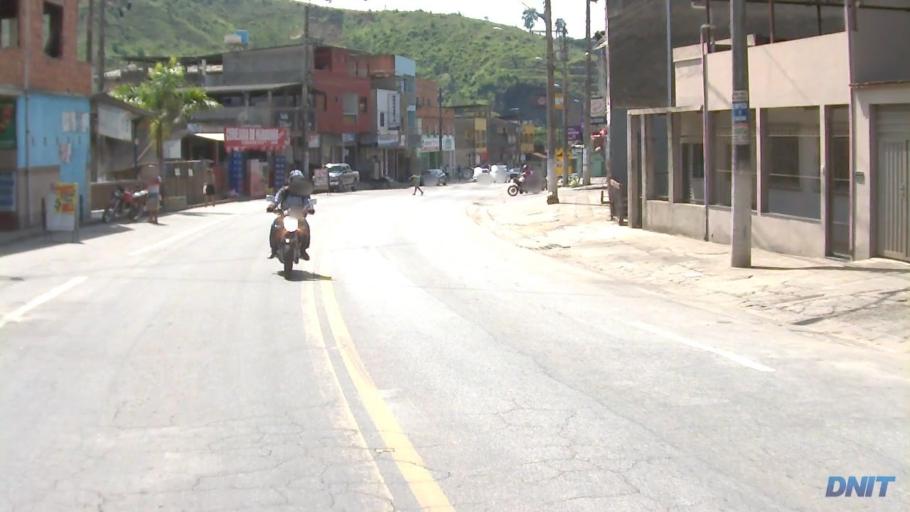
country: BR
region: Minas Gerais
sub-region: Coronel Fabriciano
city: Coronel Fabriciano
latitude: -19.5334
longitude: -42.6680
